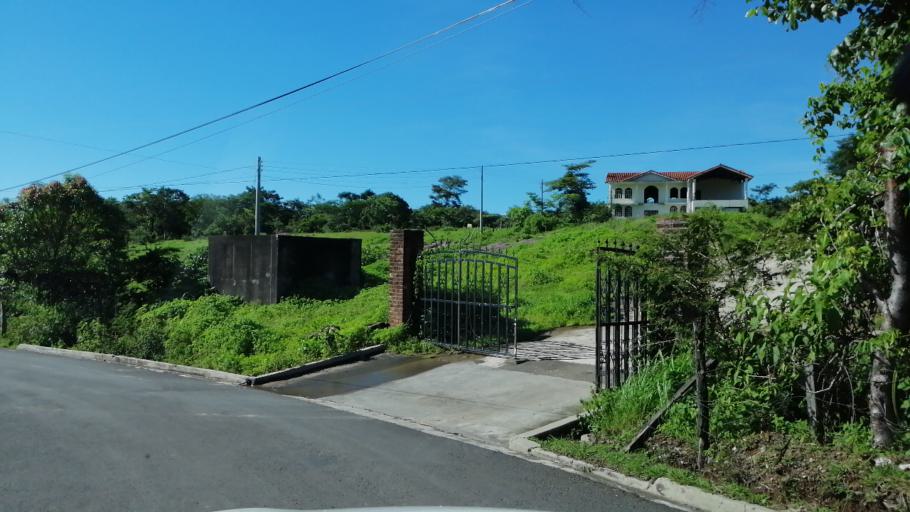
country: SV
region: Morazan
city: Corinto
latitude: 13.8095
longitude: -87.9773
